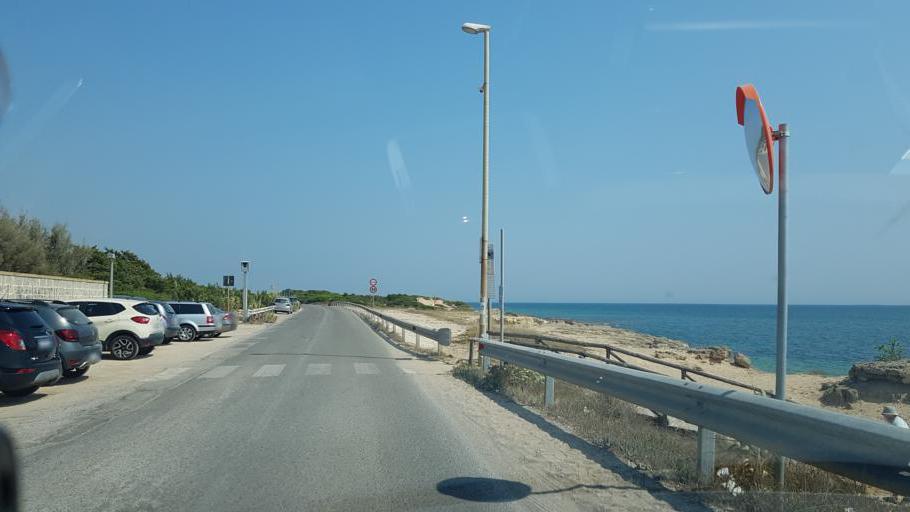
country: IT
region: Apulia
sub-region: Provincia di Taranto
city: Maruggio
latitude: 40.2997
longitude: 17.5812
